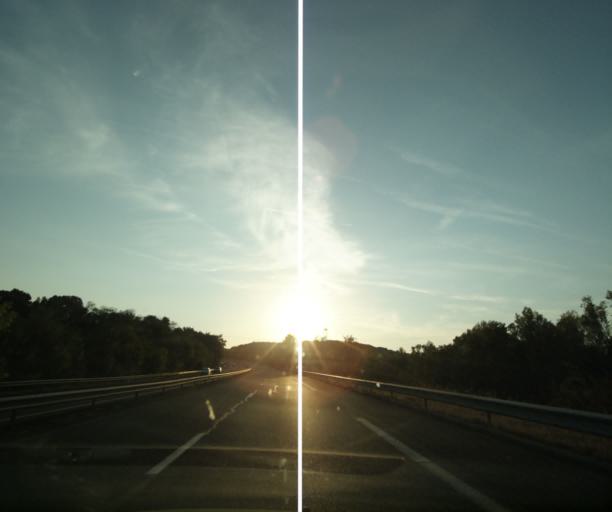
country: FR
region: Aquitaine
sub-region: Departement du Lot-et-Garonne
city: Layrac
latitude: 44.1432
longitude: 0.6544
